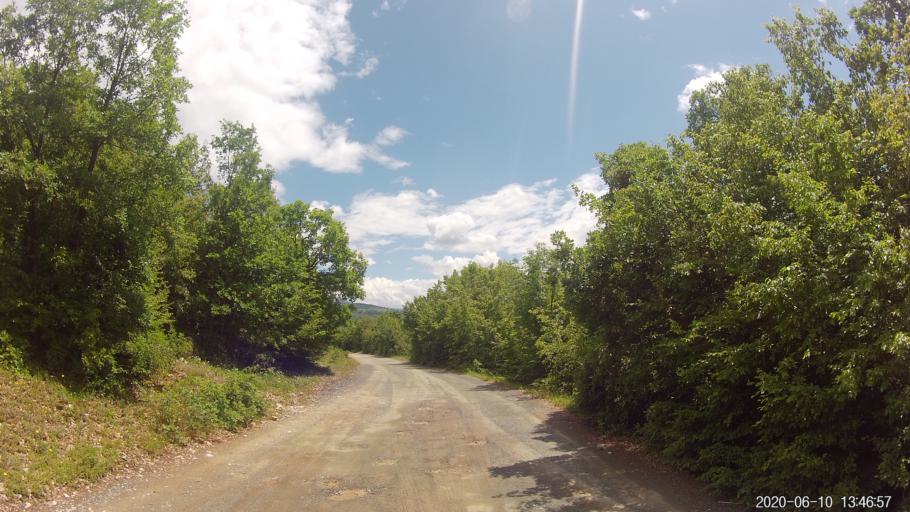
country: XK
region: Prizren
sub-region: Komuna e Therandes
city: Budakovo
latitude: 42.4070
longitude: 20.9165
